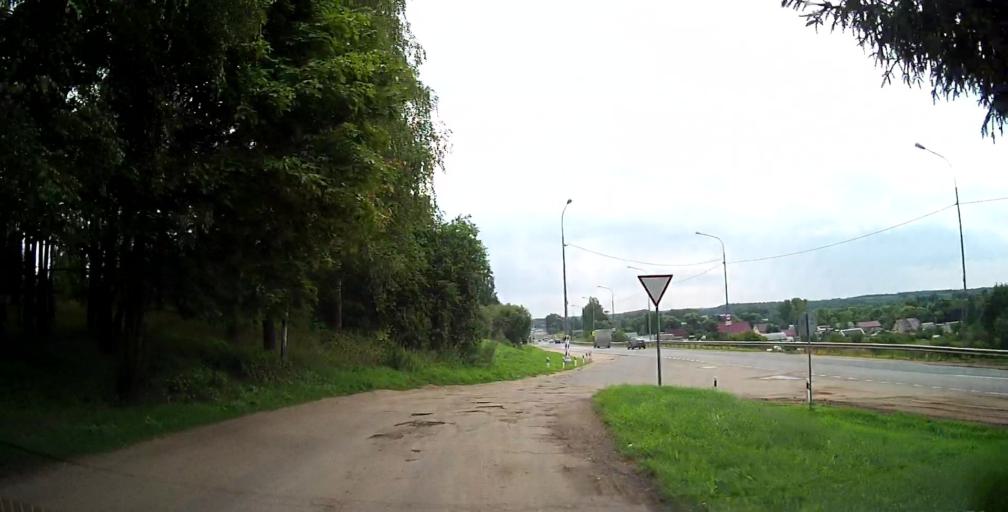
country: RU
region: Smolensk
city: Katyn'
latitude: 54.7708
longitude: 31.6835
